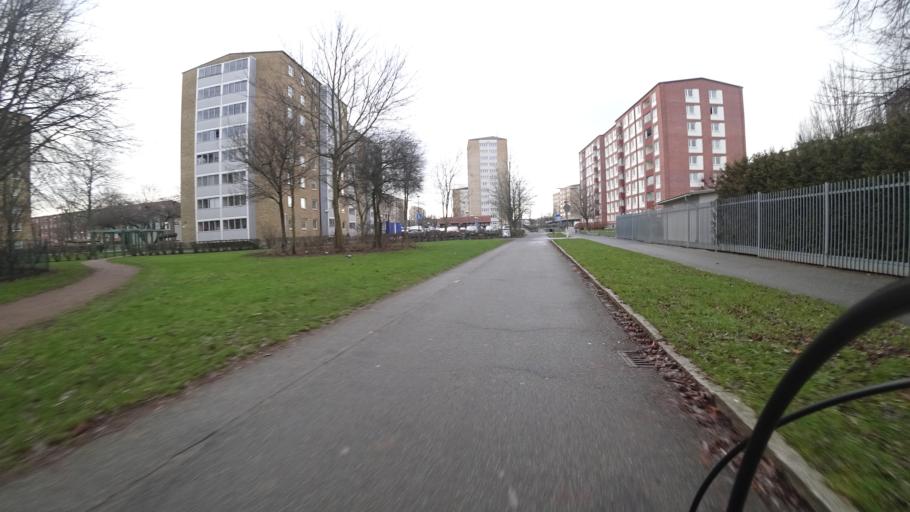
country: SE
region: Skane
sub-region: Malmo
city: Malmoe
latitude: 55.5753
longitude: 13.0221
